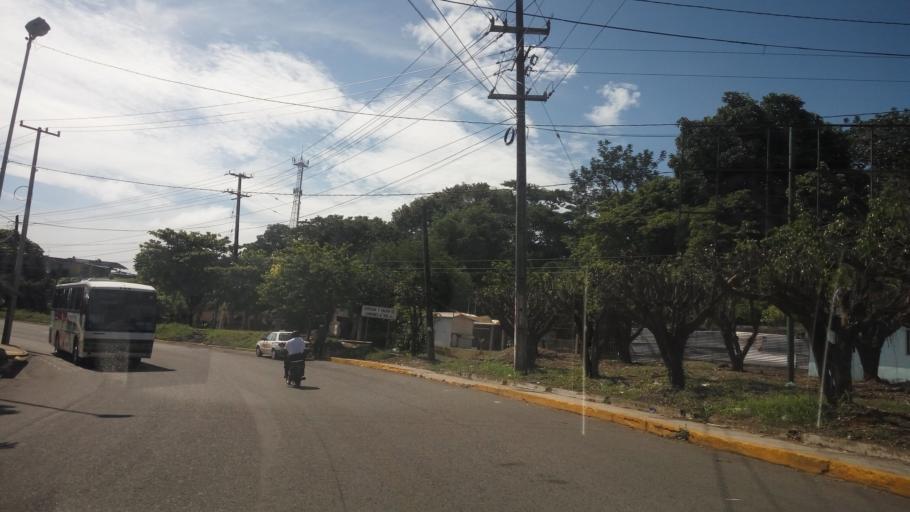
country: MX
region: Tabasco
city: Teapa
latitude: 17.5663
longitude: -92.9551
